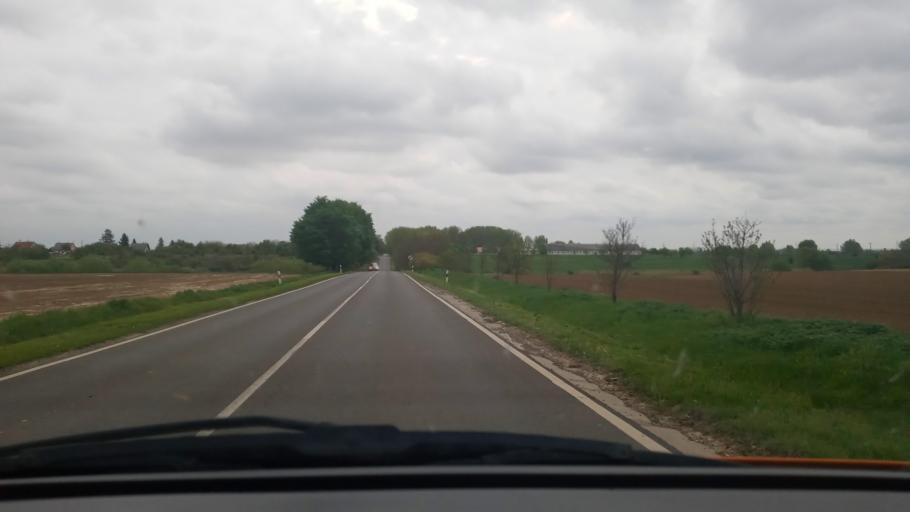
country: HU
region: Baranya
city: Boly
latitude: 45.9884
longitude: 18.5095
